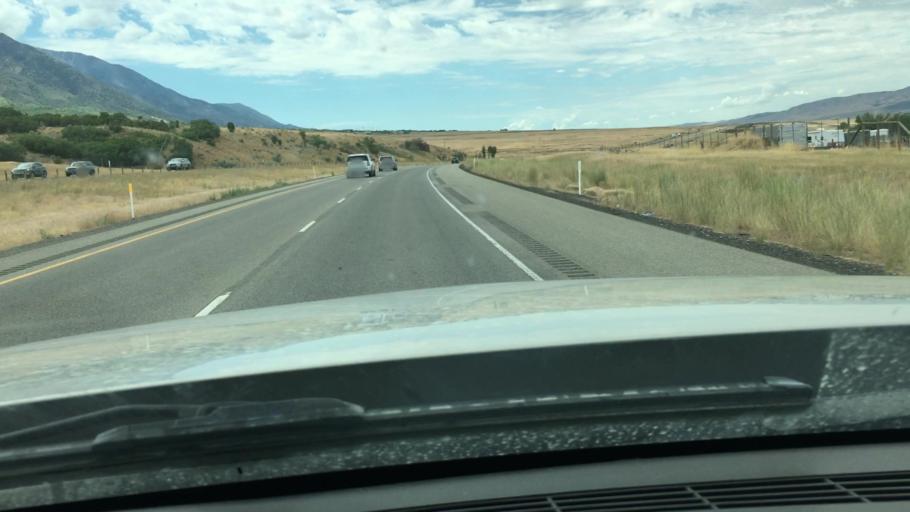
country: US
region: Utah
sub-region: Utah County
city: Santaquin
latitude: 39.9257
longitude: -111.8109
